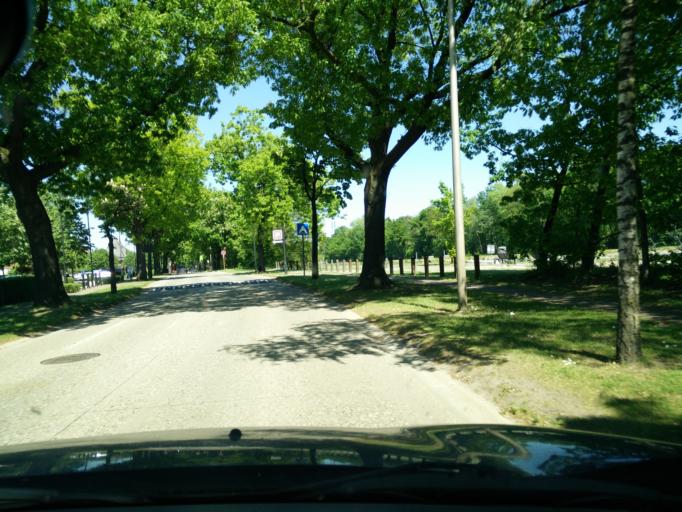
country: BE
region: Flanders
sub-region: Provincie Limburg
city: Maasmechelen
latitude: 51.0012
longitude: 5.7102
